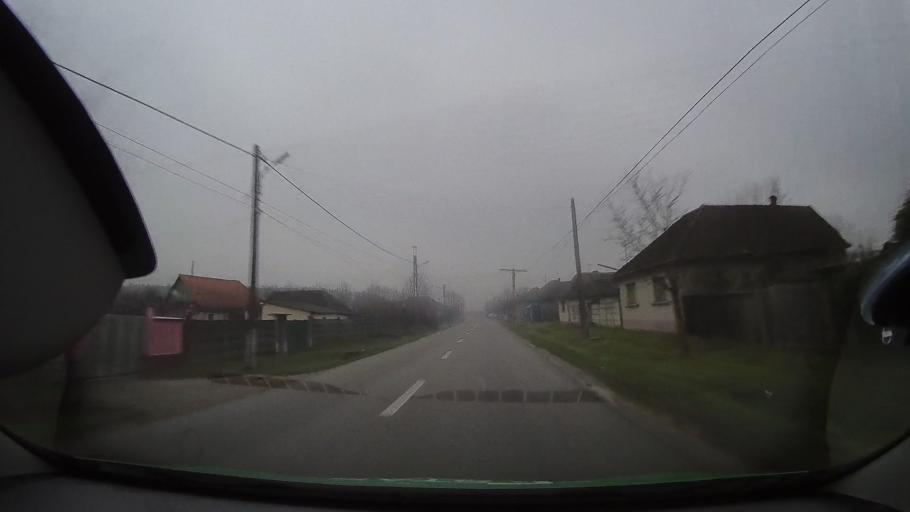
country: RO
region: Bihor
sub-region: Comuna Tinca
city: Gurbediu
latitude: 46.7864
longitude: 21.8674
